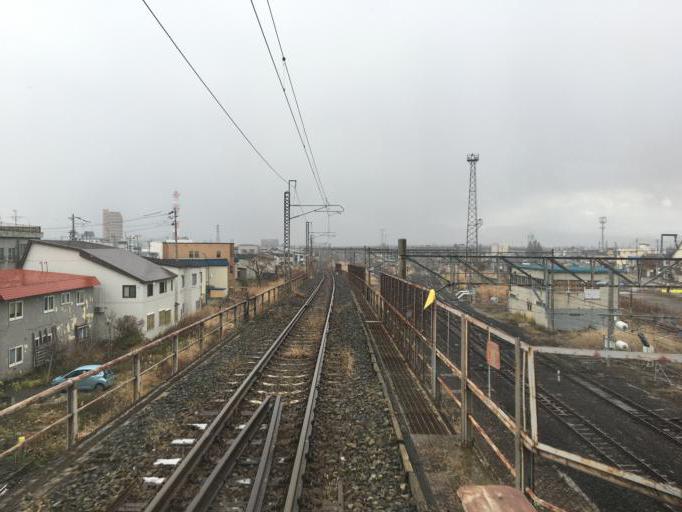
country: JP
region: Aomori
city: Aomori Shi
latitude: 40.8201
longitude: 140.7356
